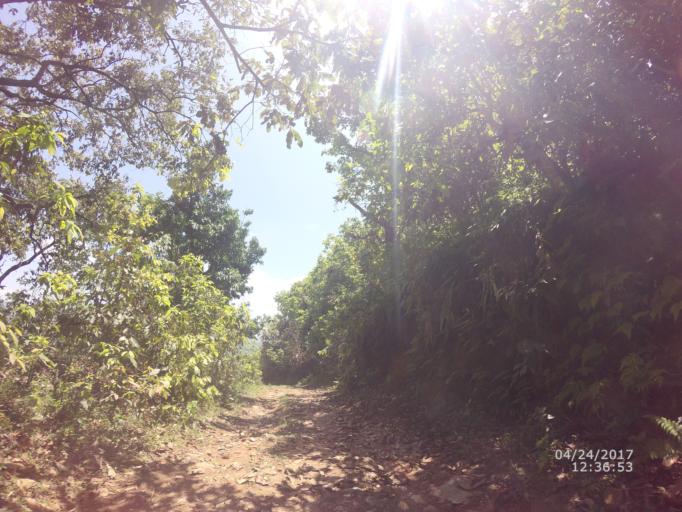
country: NP
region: Western Region
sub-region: Gandaki Zone
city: Pokhara
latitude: 28.1870
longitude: 84.0883
